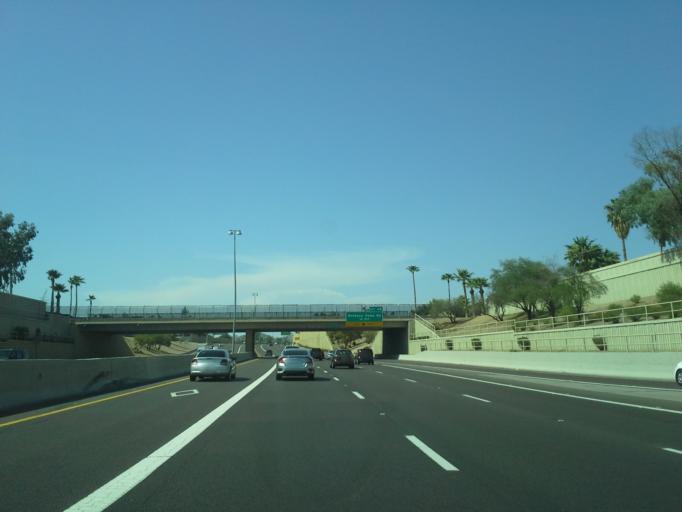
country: US
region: Arizona
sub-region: Maricopa County
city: Phoenix
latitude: 33.5155
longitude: -112.0436
